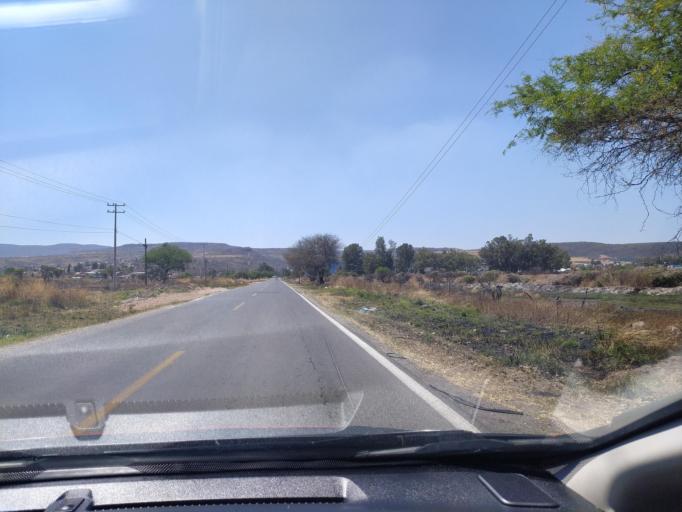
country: MX
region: Guanajuato
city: Ciudad Manuel Doblado
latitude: 20.7395
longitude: -101.9469
